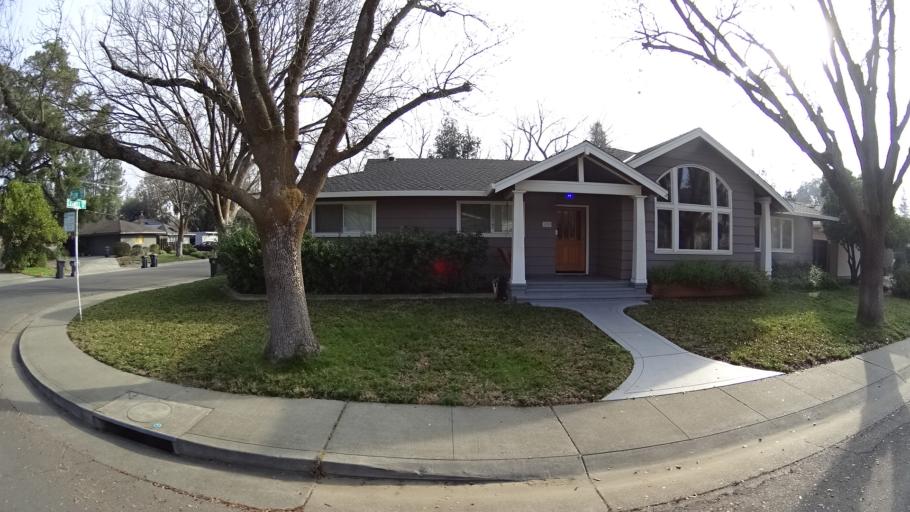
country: US
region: California
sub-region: Yolo County
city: Davis
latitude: 38.5532
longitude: -121.7659
